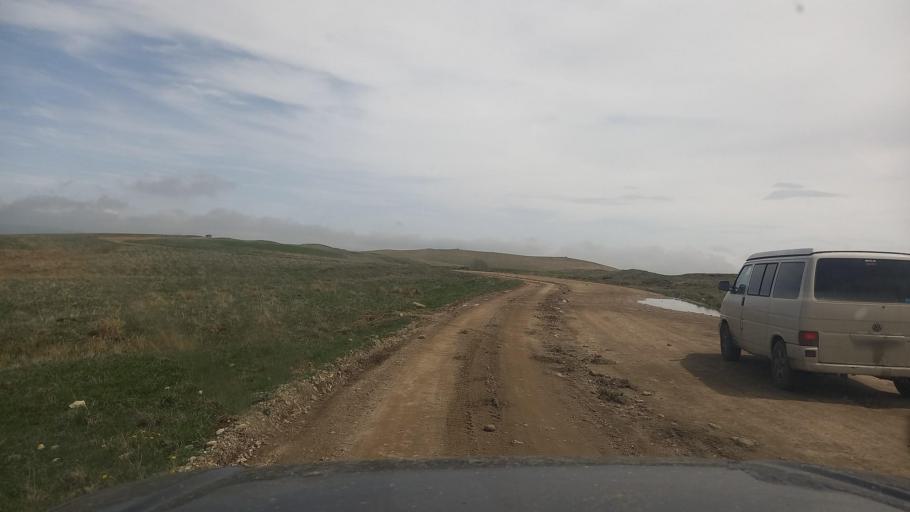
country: RU
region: Stavropol'skiy
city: Kislovodsk
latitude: 43.7644
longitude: 42.8131
